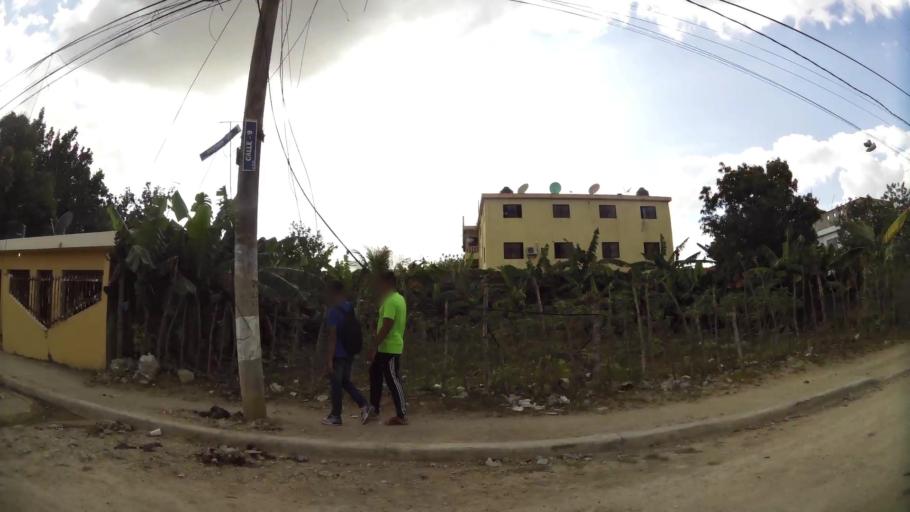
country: DO
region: Nacional
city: Ensanche Luperon
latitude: 18.5592
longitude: -69.9010
